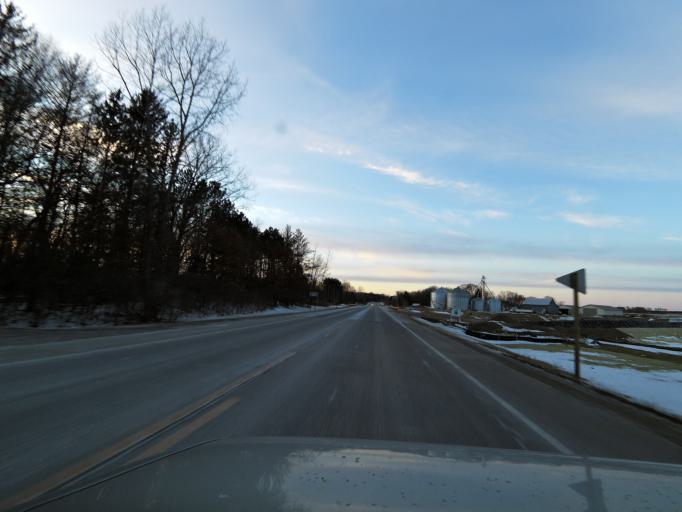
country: US
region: Minnesota
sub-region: Washington County
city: Oak Park Heights
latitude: 45.0461
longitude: -92.7787
